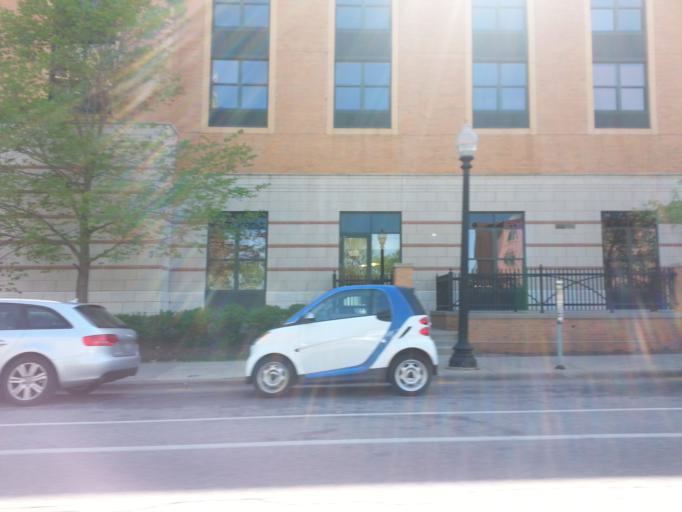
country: US
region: Minnesota
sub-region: Hennepin County
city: Minneapolis
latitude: 44.9804
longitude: -93.2621
